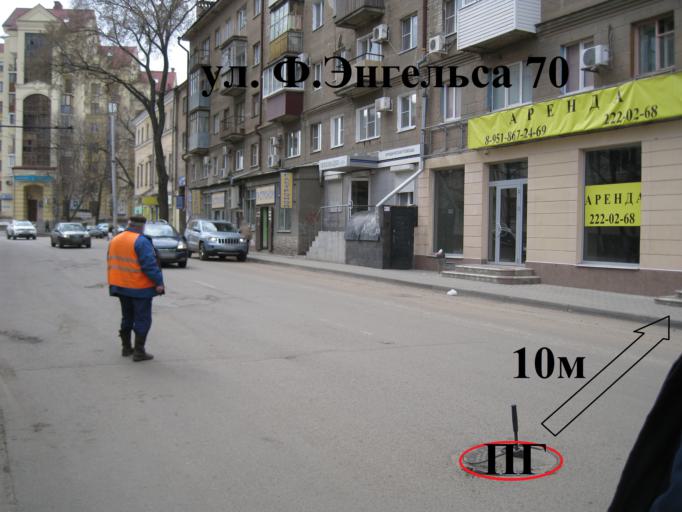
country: RU
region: Voronezj
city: Voronezh
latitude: 51.6622
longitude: 39.1922
